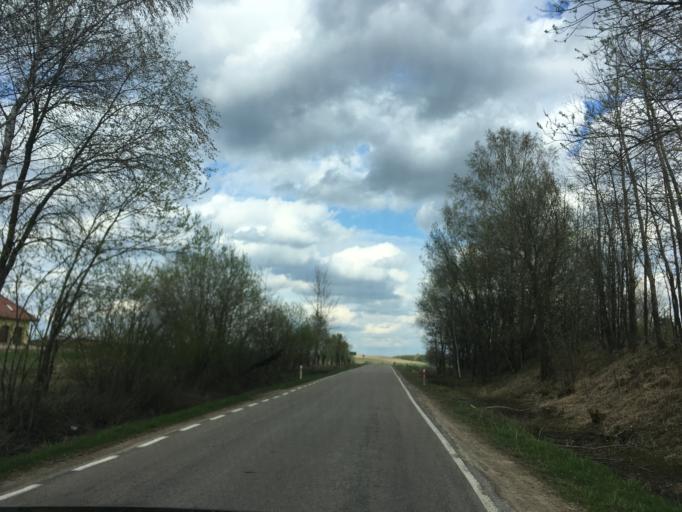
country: LT
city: Virbalis
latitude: 54.3634
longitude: 22.8313
